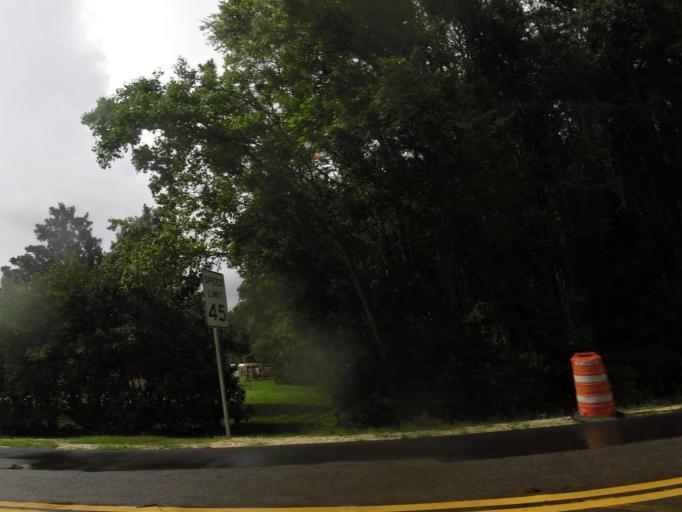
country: US
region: Florida
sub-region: Saint Johns County
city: Saint Augustine South
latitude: 29.8621
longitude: -81.3884
